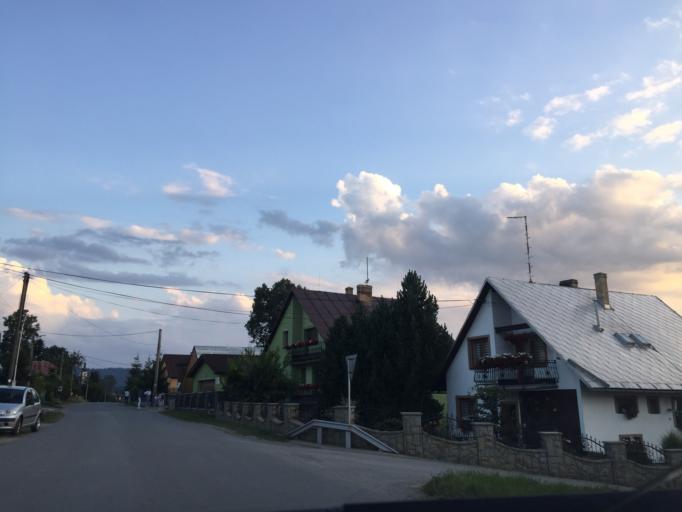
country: PL
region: Silesian Voivodeship
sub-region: Powiat zywiecki
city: Korbielow
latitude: 49.4766
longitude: 19.3828
